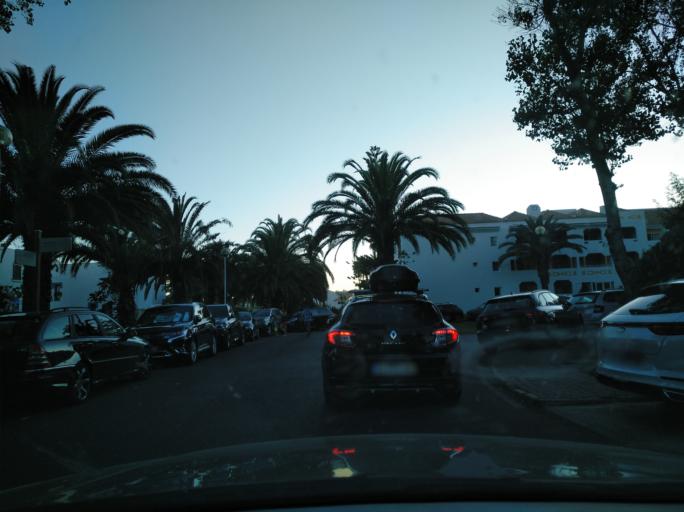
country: PT
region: Faro
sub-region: Tavira
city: Tavira
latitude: 37.1338
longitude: -7.6043
